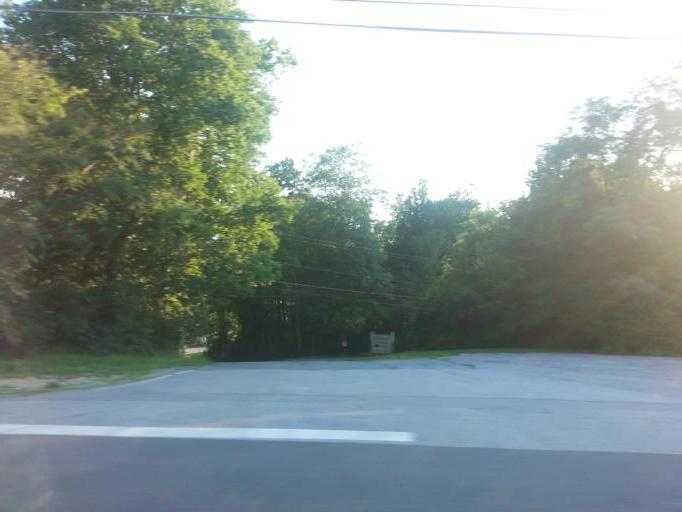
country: US
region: Tennessee
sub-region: Anderson County
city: Clinton
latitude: 36.0252
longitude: -84.0603
